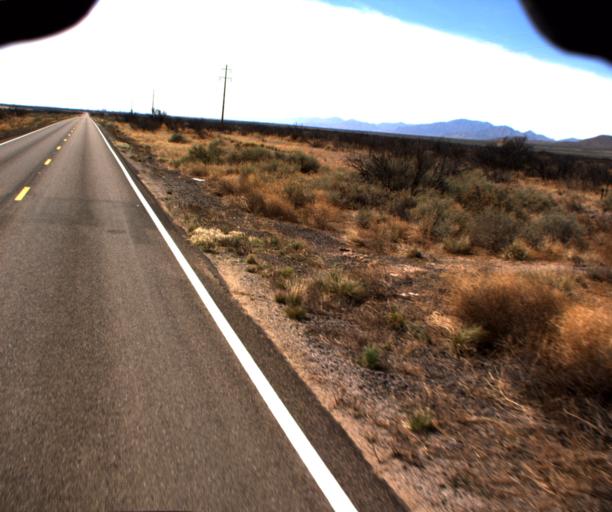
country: US
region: Arizona
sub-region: Cochise County
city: Willcox
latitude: 32.1624
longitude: -109.9424
